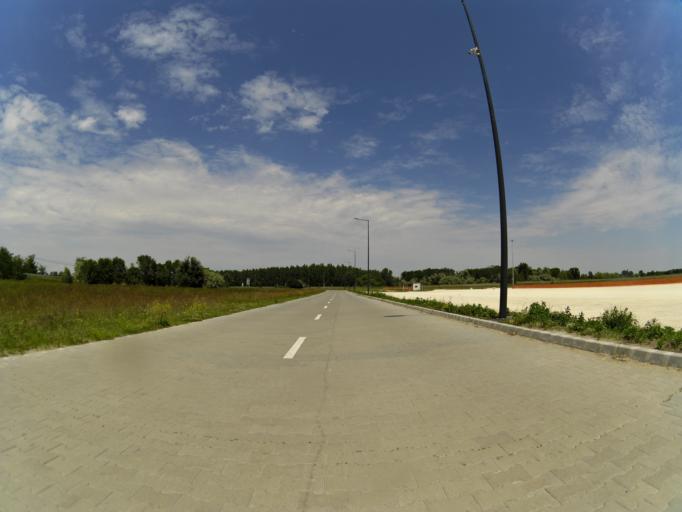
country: HU
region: Csongrad
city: Balastya
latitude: 46.4056
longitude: 19.9754
